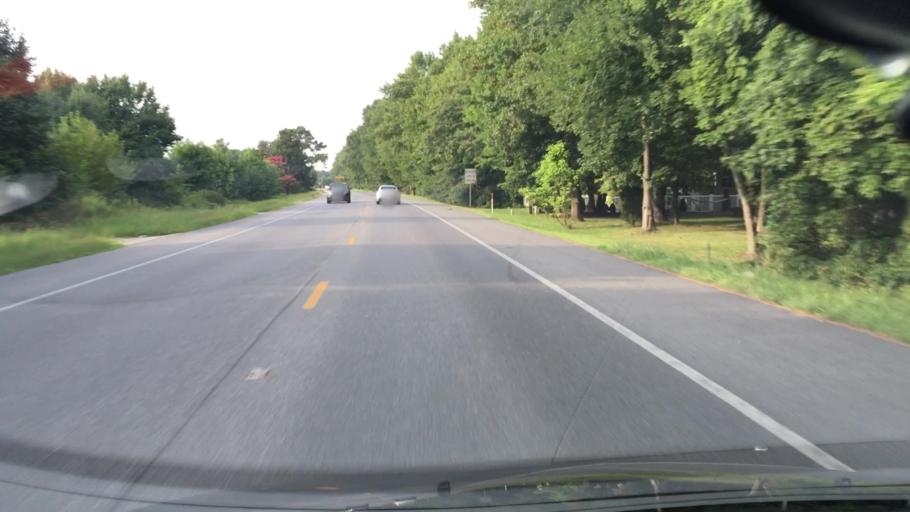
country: US
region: Maryland
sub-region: Worcester County
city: Ocean Pines
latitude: 38.3687
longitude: -75.1647
